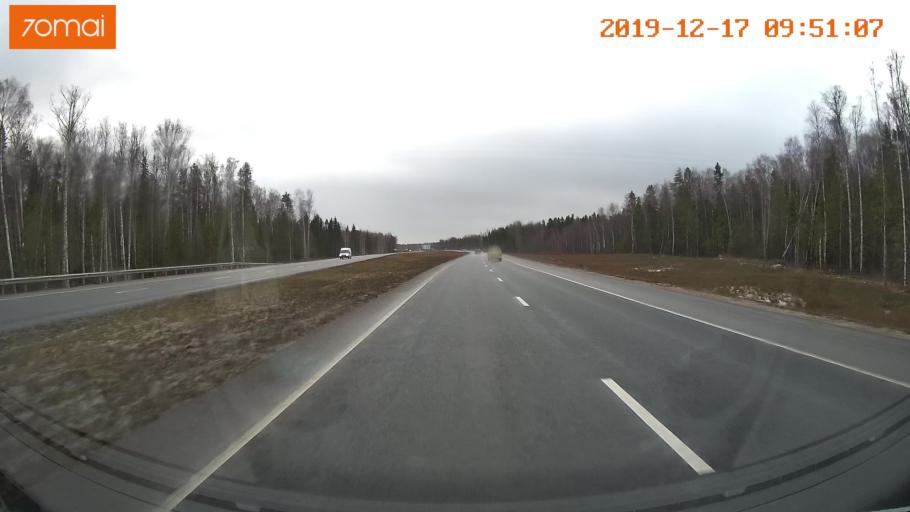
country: RU
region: Vladimir
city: Kommunar
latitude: 56.0486
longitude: 40.5173
